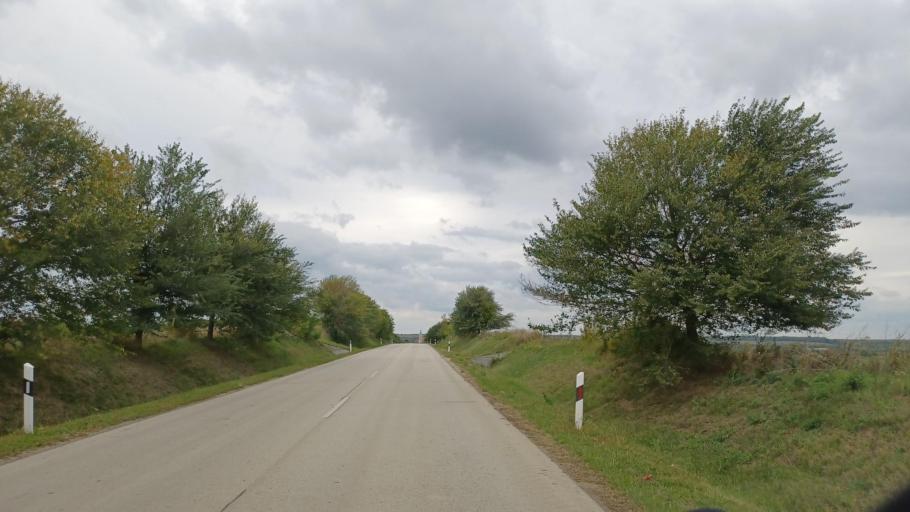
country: HU
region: Tolna
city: Simontornya
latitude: 46.7399
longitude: 18.5627
